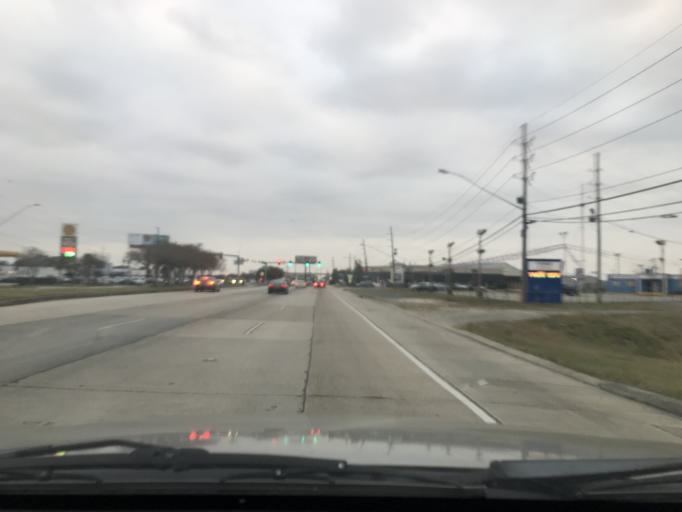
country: US
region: Louisiana
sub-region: Jefferson Parish
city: Woodmere
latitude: 29.8721
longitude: -90.0808
